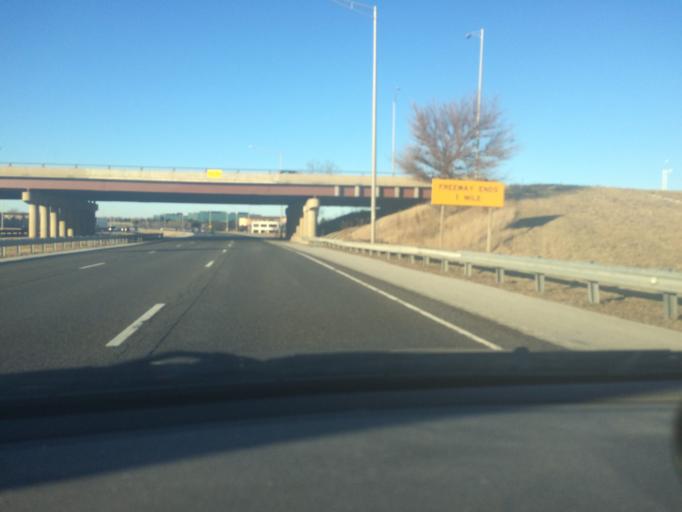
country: US
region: Illinois
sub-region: Lake County
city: Long Grove
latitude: 42.1384
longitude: -88.0047
